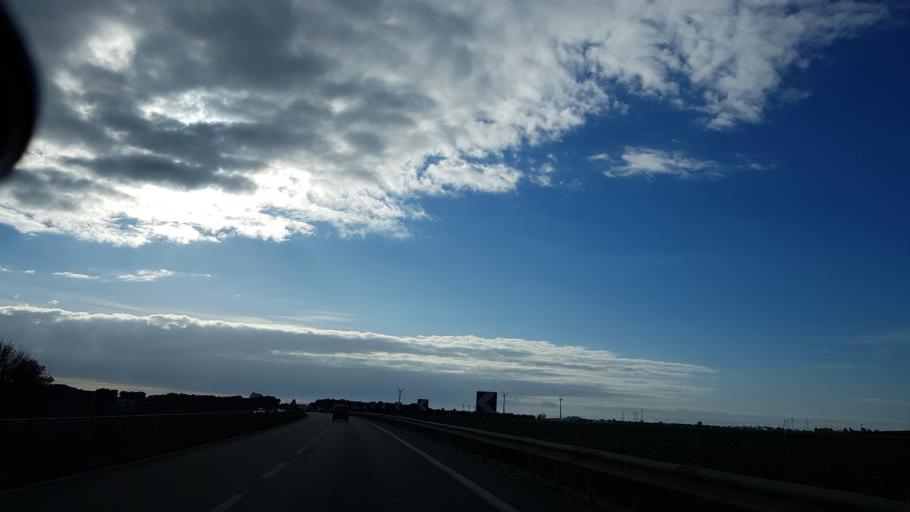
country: IT
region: Apulia
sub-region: Provincia di Brindisi
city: La Rosa
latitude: 40.5847
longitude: 17.9753
